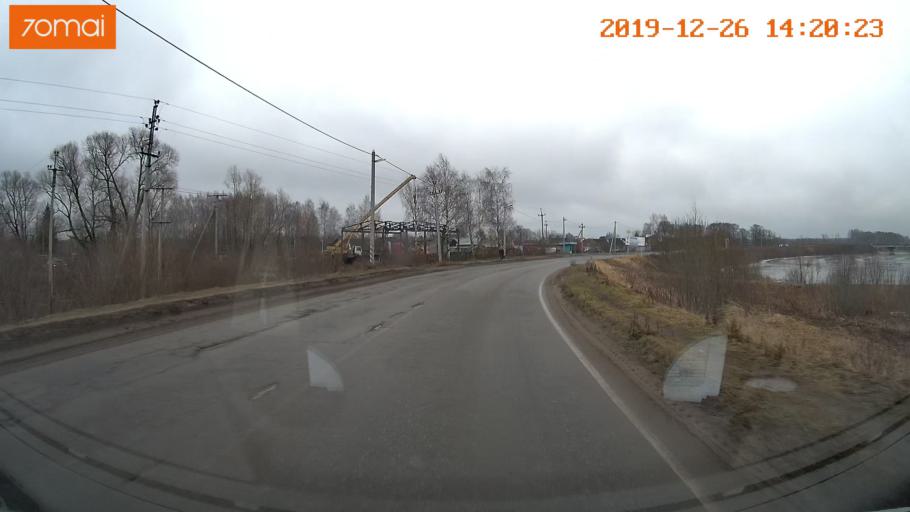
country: RU
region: Jaroslavl
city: Poshekhon'ye
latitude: 58.5101
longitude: 39.1296
